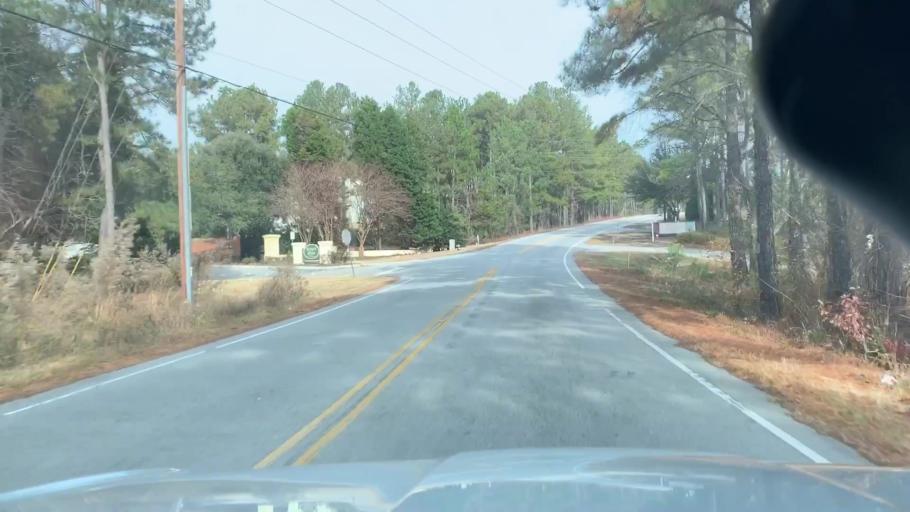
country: US
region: South Carolina
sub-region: Richland County
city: Woodfield
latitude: 34.0937
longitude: -80.8927
